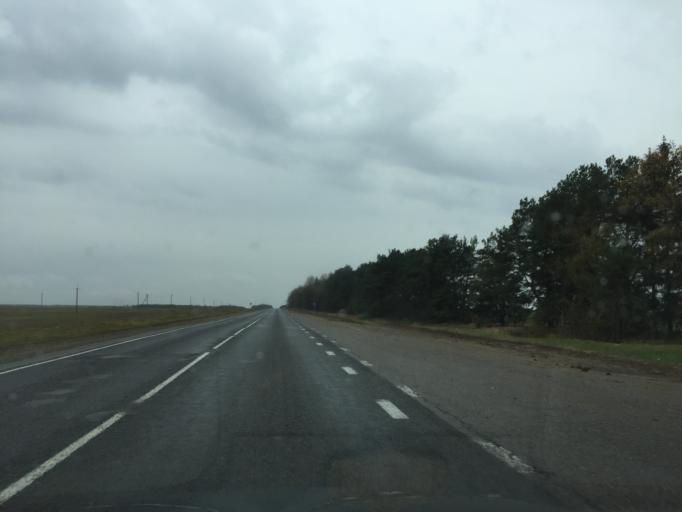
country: BY
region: Mogilev
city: Slawharad
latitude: 53.3949
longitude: 30.9102
